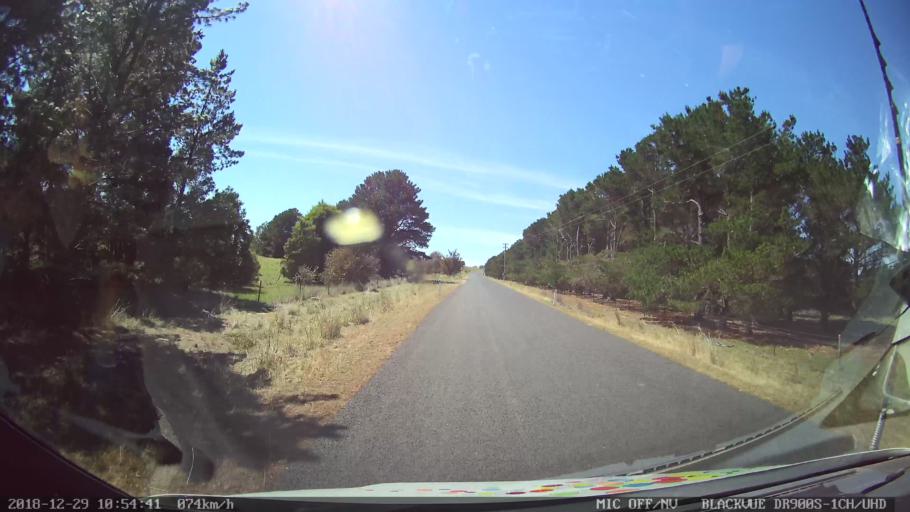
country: AU
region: New South Wales
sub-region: Palerang
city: Bungendore
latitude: -35.1169
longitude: 149.5287
